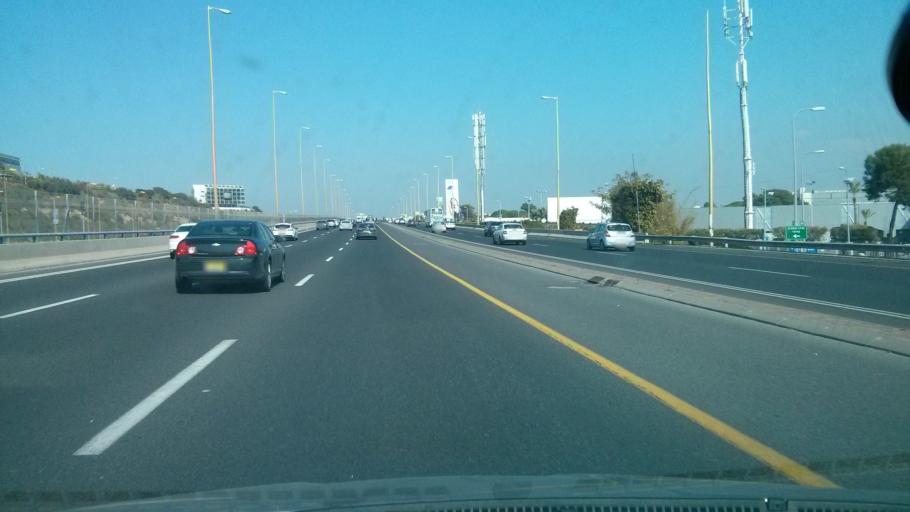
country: IL
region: Tel Aviv
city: Ramat Gan
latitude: 32.1039
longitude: 34.8051
